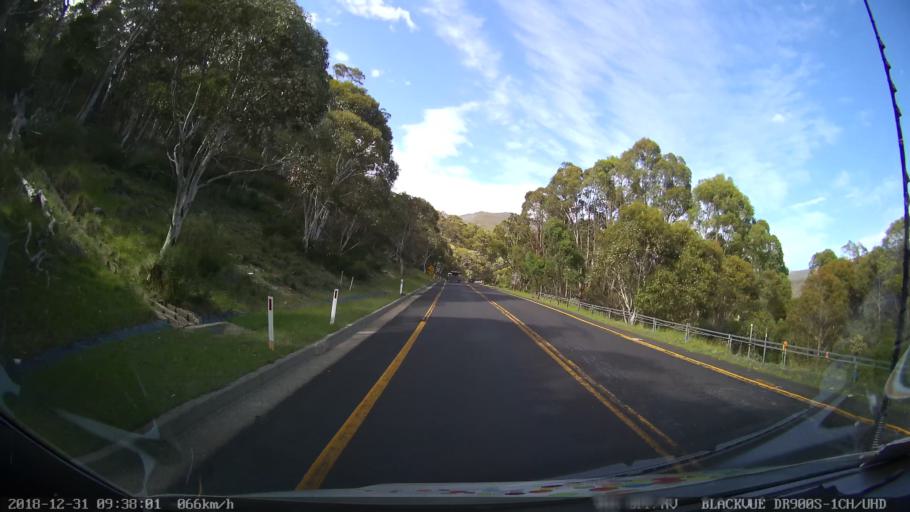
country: AU
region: New South Wales
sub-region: Snowy River
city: Jindabyne
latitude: -36.4712
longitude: 148.3714
